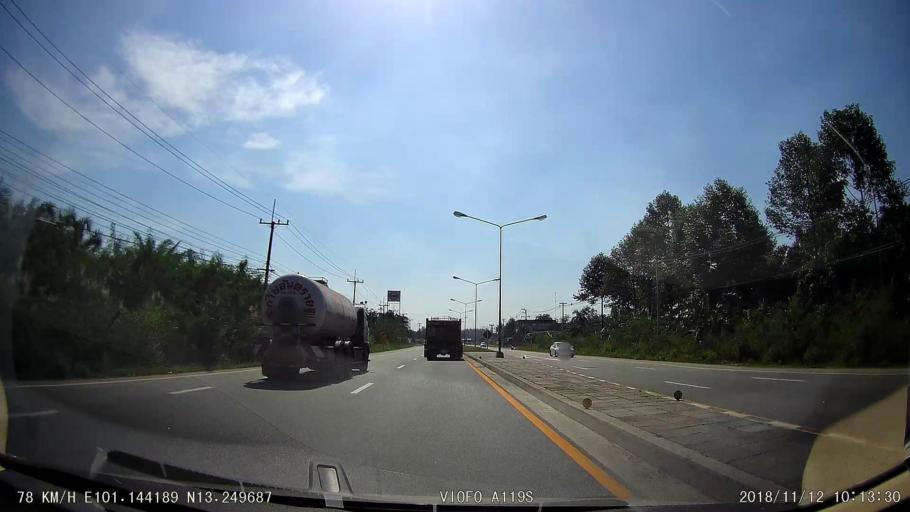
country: TH
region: Chon Buri
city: Ban Bueng
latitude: 13.2495
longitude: 101.1444
